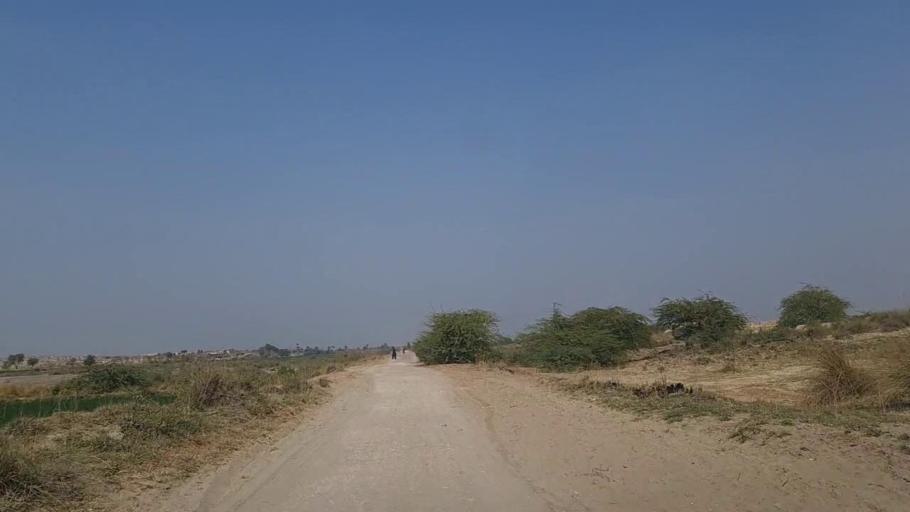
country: PK
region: Sindh
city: Daur
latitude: 26.4758
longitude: 68.4510
